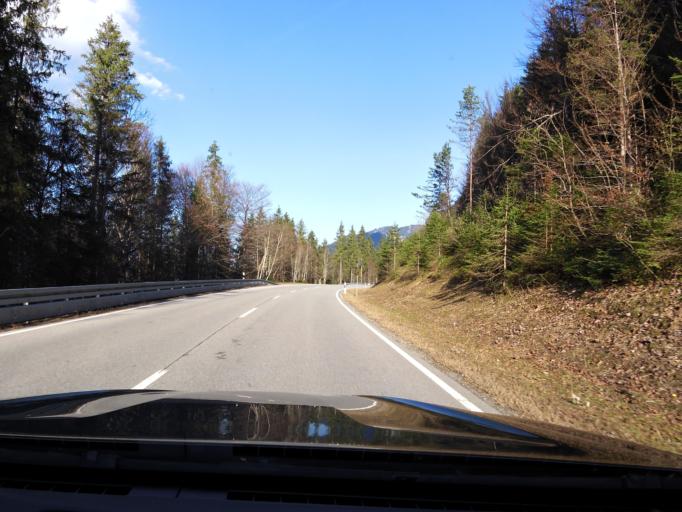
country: DE
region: Bavaria
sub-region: Upper Bavaria
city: Jachenau
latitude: 47.5585
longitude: 11.4854
